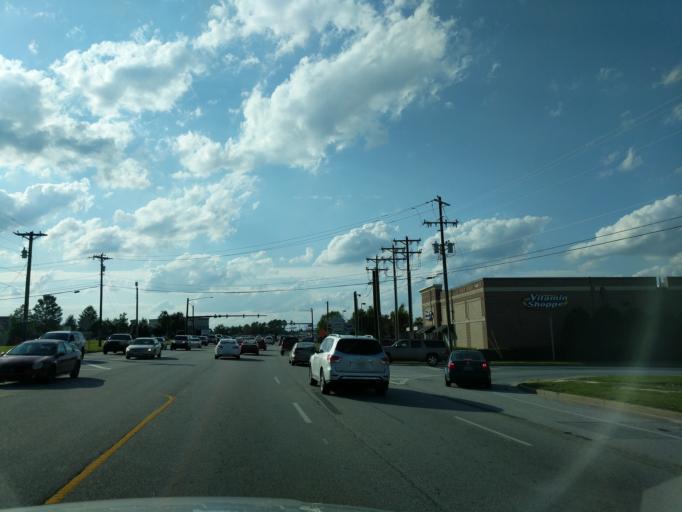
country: US
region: South Carolina
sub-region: Greenville County
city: Mauldin
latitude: 34.8258
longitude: -82.2969
